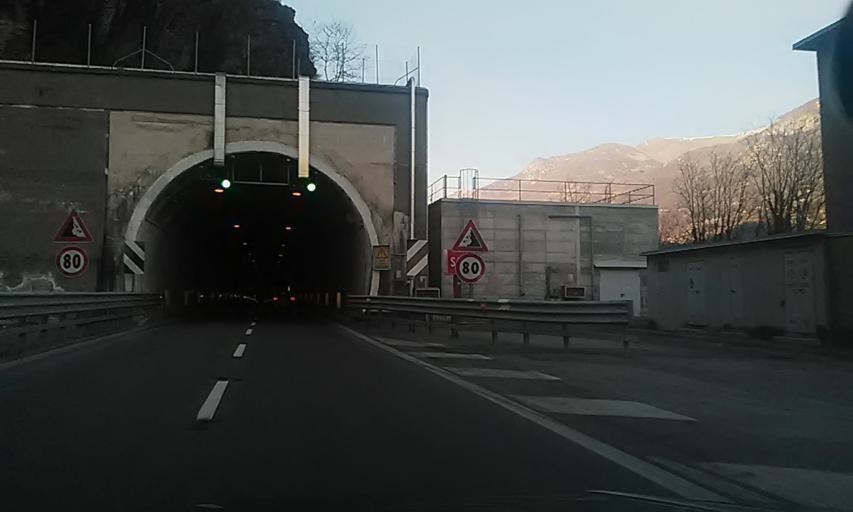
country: IT
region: Piedmont
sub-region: Provincia di Torino
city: Quassolo
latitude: 45.5289
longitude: 7.8331
